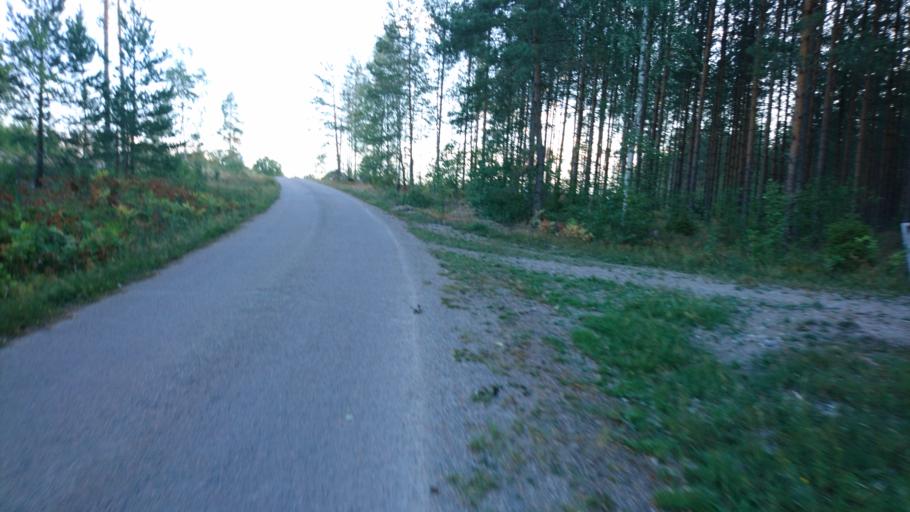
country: SE
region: Soedermanland
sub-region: Strangnas Kommun
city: Stallarholmen
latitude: 59.4019
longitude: 17.3130
